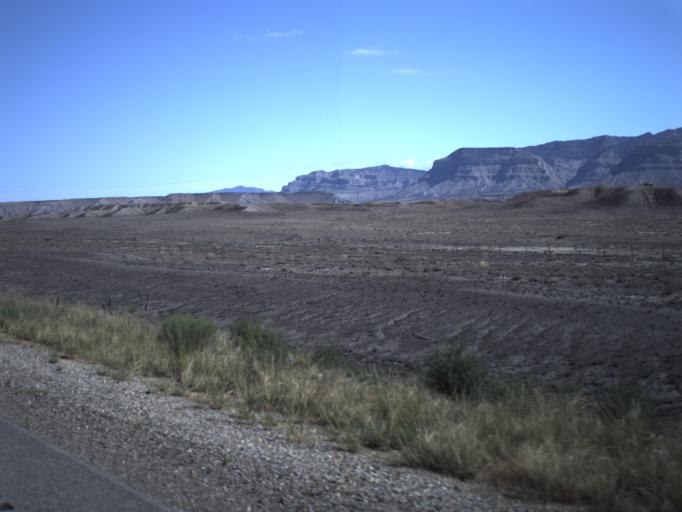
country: US
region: Utah
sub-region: Carbon County
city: East Carbon City
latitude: 39.3497
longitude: -110.3791
